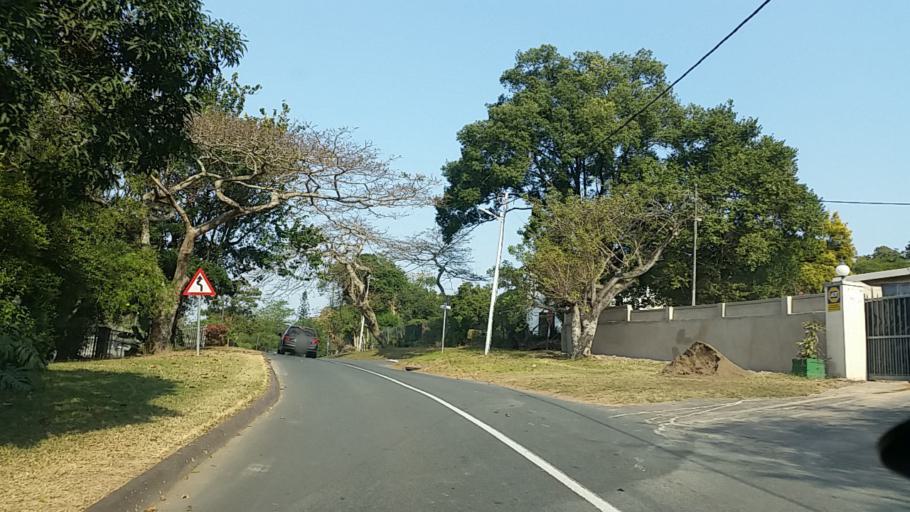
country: ZA
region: KwaZulu-Natal
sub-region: eThekwini Metropolitan Municipality
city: Berea
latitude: -29.8342
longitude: 30.9360
